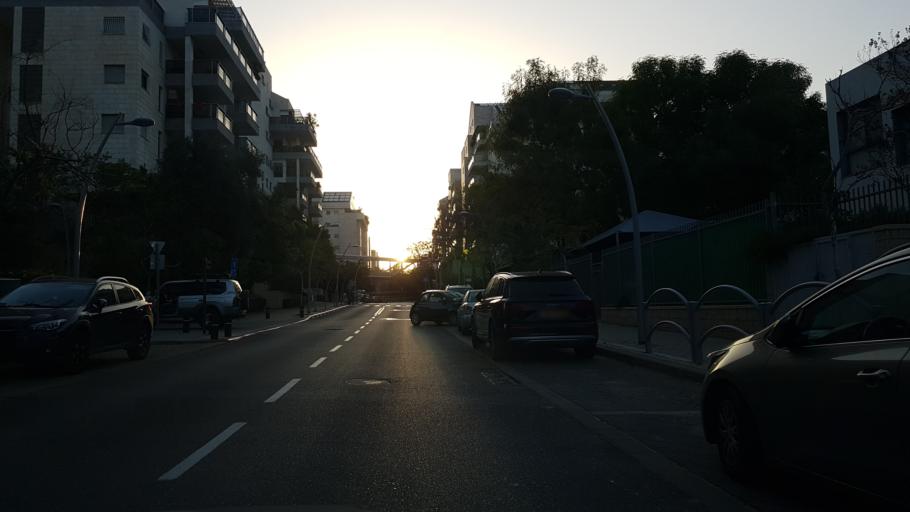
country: IL
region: Central District
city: Kfar Saba
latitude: 32.1951
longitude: 34.8949
